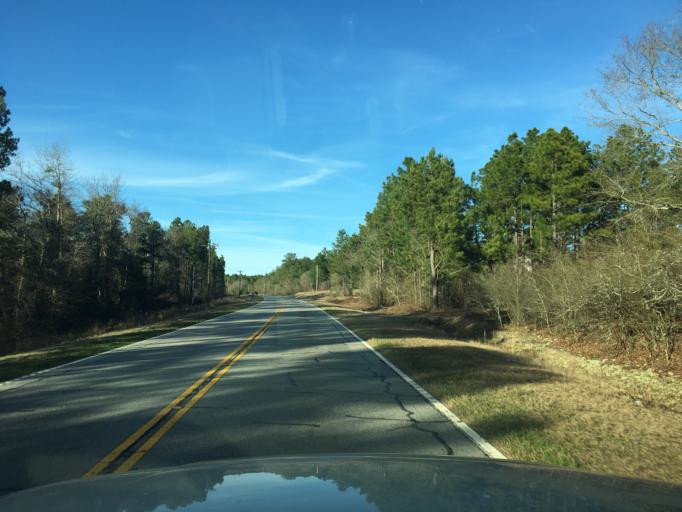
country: US
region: South Carolina
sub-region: Edgefield County
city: Johnston
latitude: 33.7432
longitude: -81.6451
